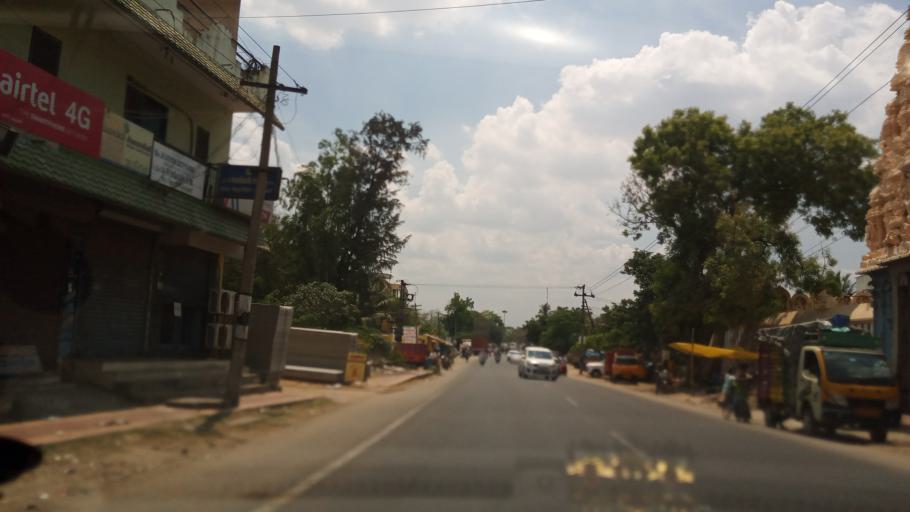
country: IN
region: Tamil Nadu
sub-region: Vellore
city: Walajapet
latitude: 12.9255
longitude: 79.3599
